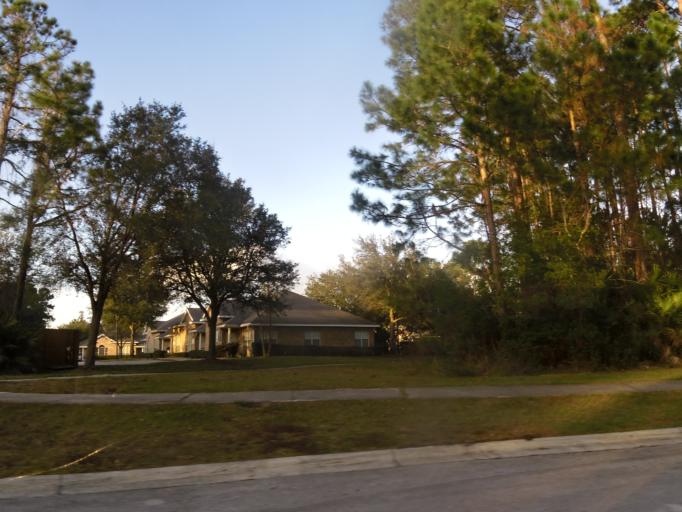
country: US
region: Florida
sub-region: Saint Johns County
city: Ponte Vedra Beach
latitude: 30.2556
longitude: -81.4619
